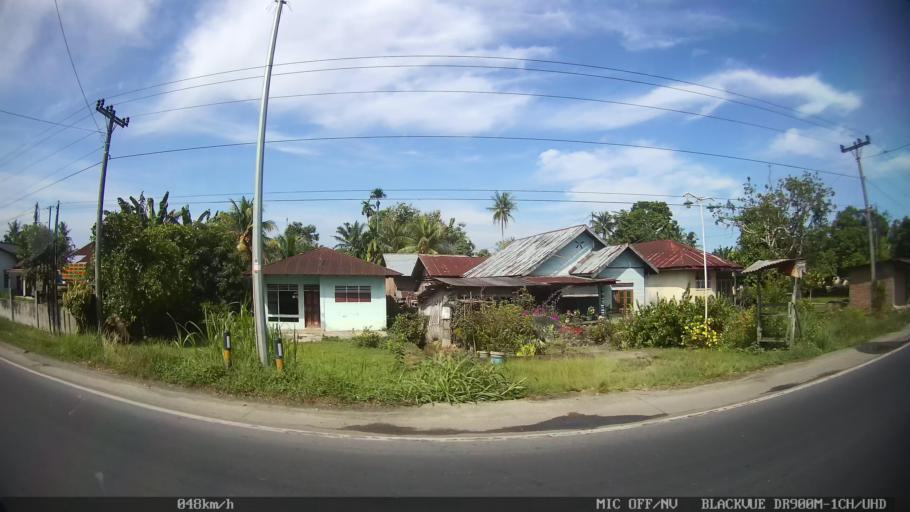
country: ID
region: North Sumatra
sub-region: Kabupaten Langkat
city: Stabat
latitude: 3.7218
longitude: 98.5022
